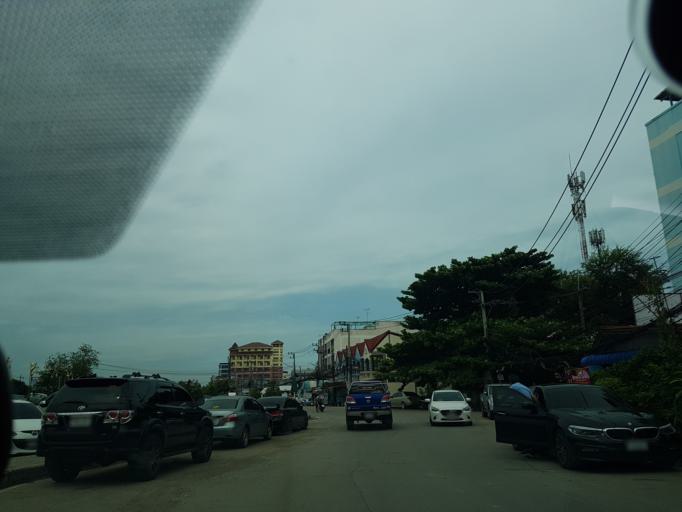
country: TH
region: Bangkok
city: Sai Mai
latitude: 13.9849
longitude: 100.6222
